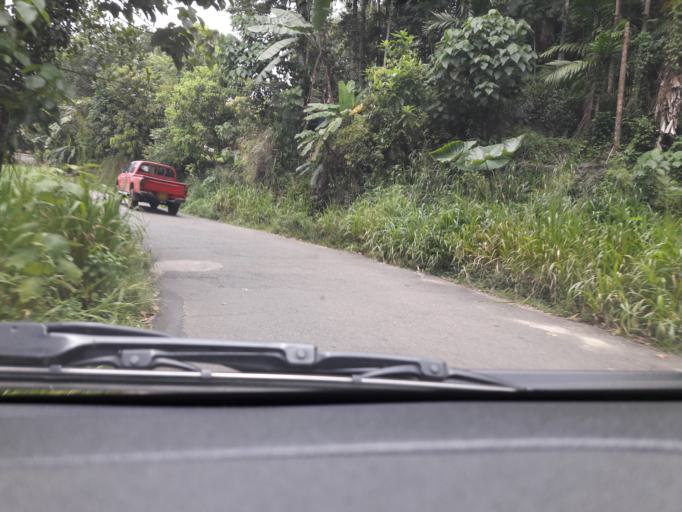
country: LK
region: Southern
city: Galle
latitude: 6.1986
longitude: 80.3016
